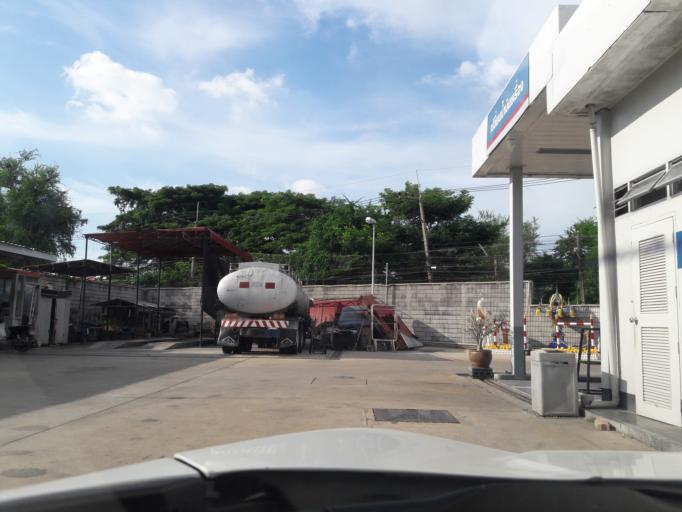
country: TH
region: Lop Buri
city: Ban Mi
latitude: 15.0439
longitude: 100.5453
